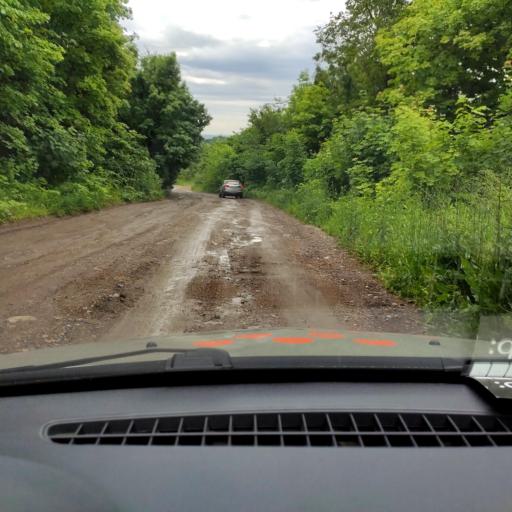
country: RU
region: Bashkortostan
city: Iglino
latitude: 54.8894
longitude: 56.2743
